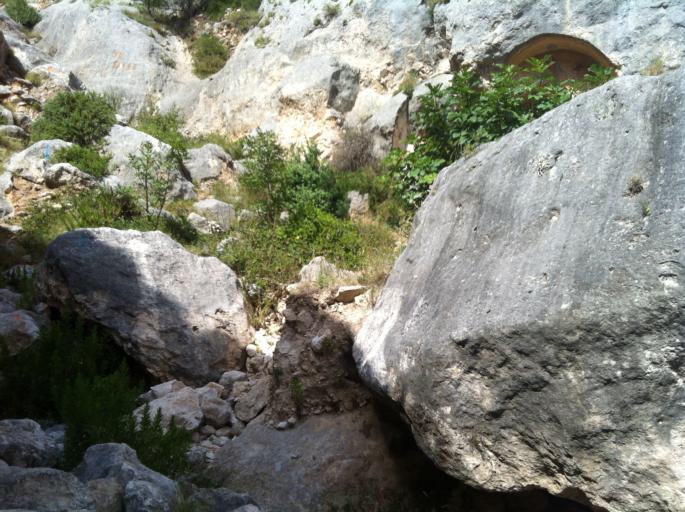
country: IT
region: Apulia
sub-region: Provincia di Foggia
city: Manfredonia
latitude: 41.6735
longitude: 15.9113
